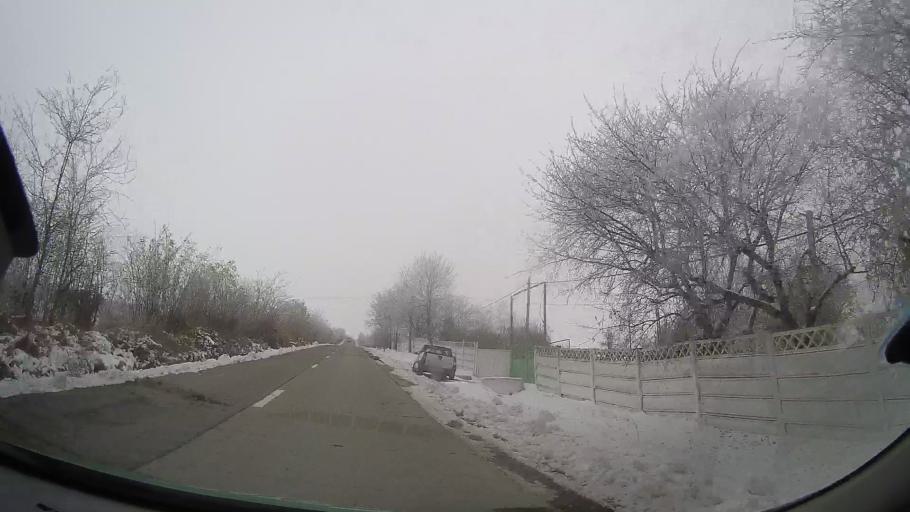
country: RO
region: Bacau
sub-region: Comuna Podu Turcului
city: Podu Turcului
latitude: 46.2061
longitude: 27.3988
